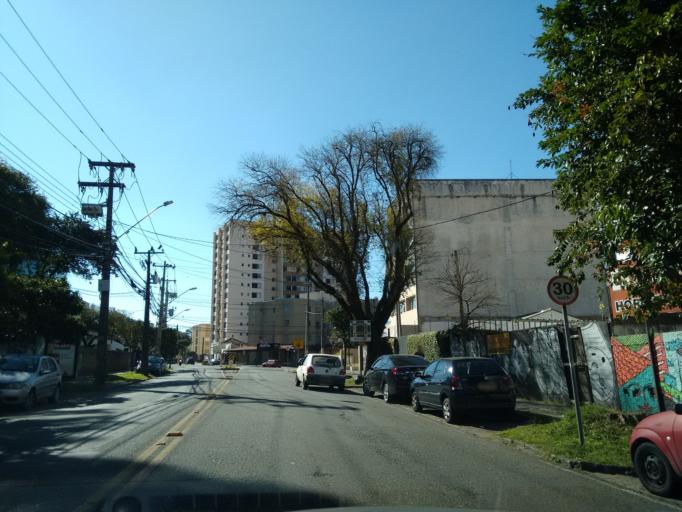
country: BR
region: Parana
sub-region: Curitiba
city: Curitiba
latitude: -25.4140
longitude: -49.2712
